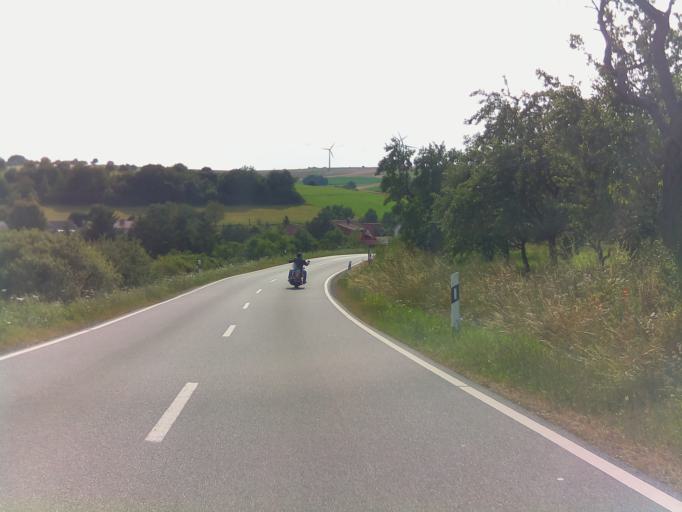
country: DE
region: Baden-Wuerttemberg
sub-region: Regierungsbezirk Stuttgart
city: Buch am Ahorn
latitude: 49.5333
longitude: 9.5135
